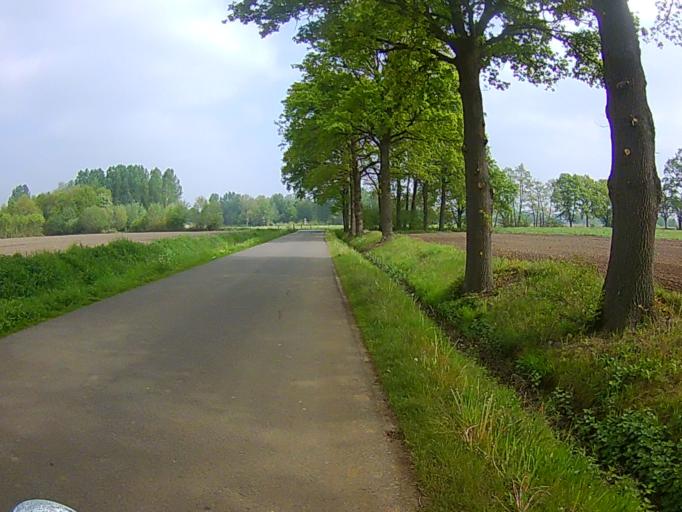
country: BE
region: Flanders
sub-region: Provincie Antwerpen
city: Zandhoven
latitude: 51.2026
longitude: 4.6875
